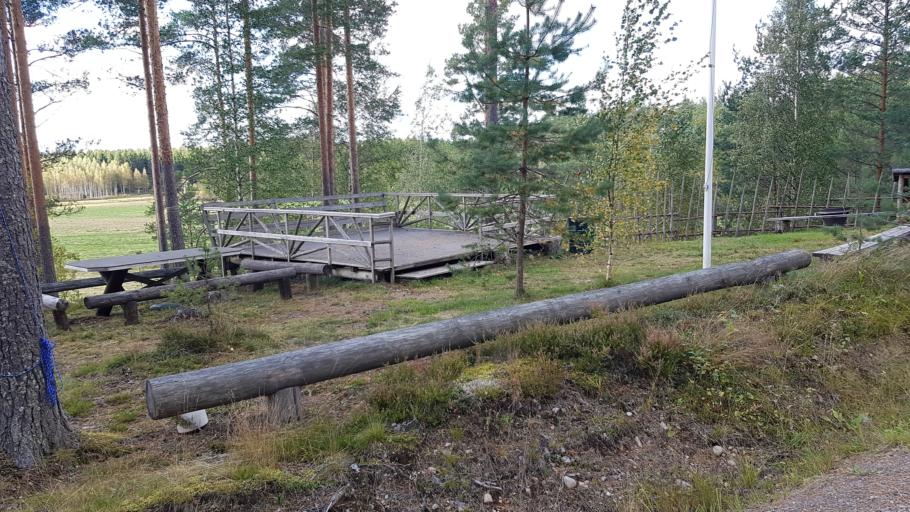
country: FI
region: South Karelia
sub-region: Imatra
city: Ruokolahti
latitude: 61.2529
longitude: 29.0972
